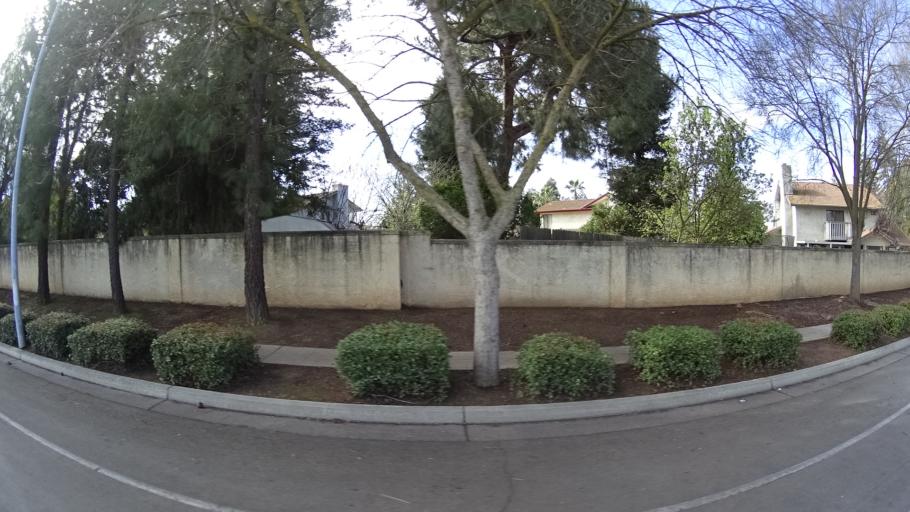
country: US
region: California
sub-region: Fresno County
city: West Park
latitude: 36.8335
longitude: -119.8648
